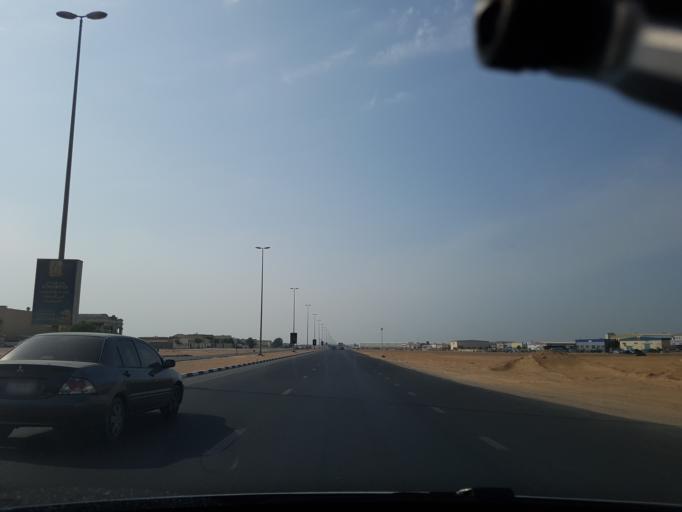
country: AE
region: Ajman
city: Ajman
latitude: 25.4283
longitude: 55.5183
